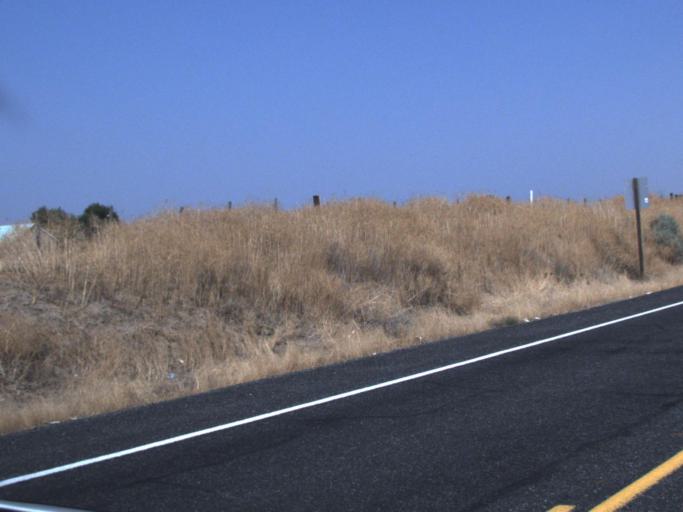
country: US
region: Washington
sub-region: Benton County
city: Prosser
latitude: 46.1931
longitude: -119.7992
